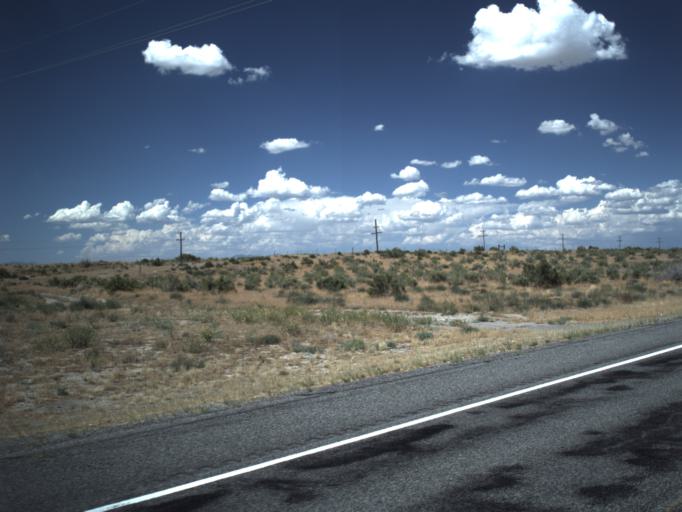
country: US
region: Utah
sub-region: Millard County
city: Delta
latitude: 39.4095
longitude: -112.4887
